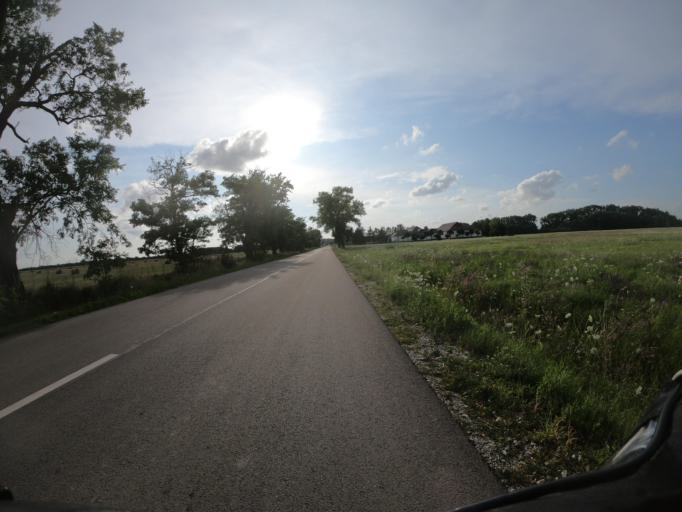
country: HU
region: Borsod-Abauj-Zemplen
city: Mezokeresztes
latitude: 47.8300
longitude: 20.7938
